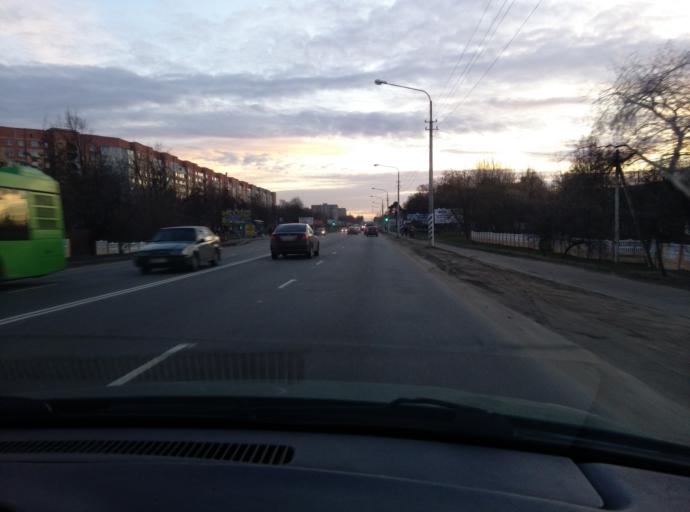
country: BY
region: Minsk
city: Horad Barysaw
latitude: 54.2246
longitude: 28.4941
